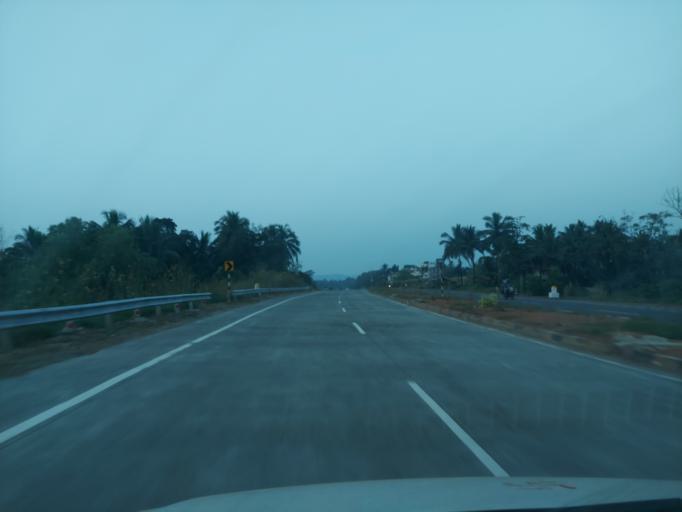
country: IN
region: Maharashtra
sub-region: Sindhudurg
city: Kudal
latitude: 16.0941
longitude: 73.7061
